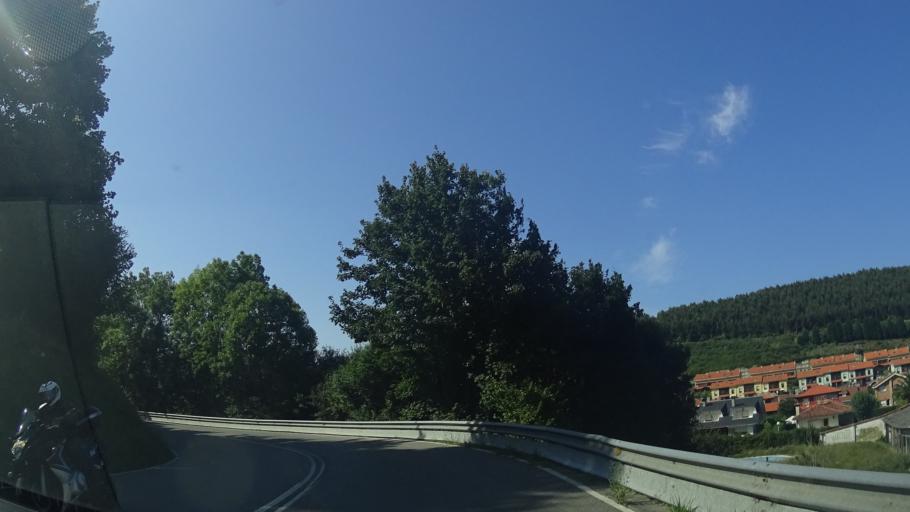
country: ES
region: Asturias
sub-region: Province of Asturias
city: Ribadesella
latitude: 43.4653
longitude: -5.0824
